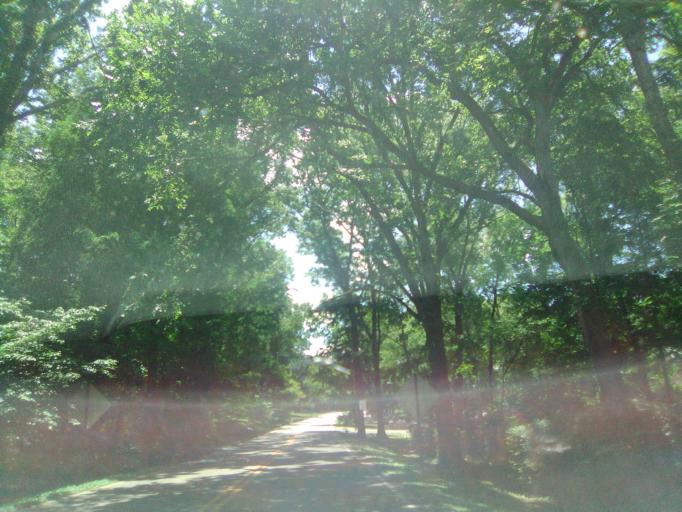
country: US
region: Tennessee
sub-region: Davidson County
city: Belle Meade
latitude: 36.1057
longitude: -86.8529
